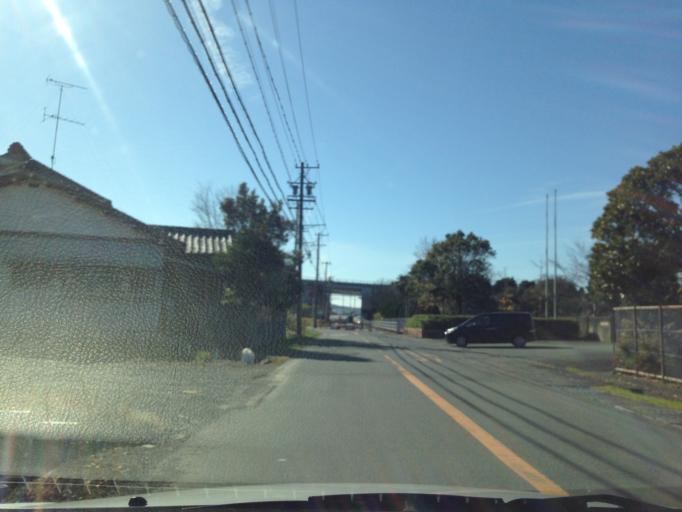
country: JP
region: Shizuoka
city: Kakegawa
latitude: 34.7664
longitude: 137.9822
